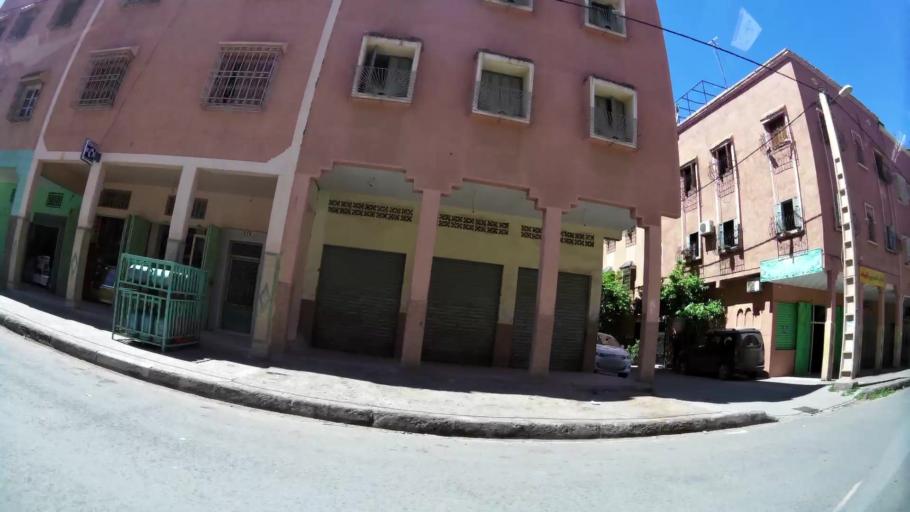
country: MA
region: Marrakech-Tensift-Al Haouz
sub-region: Marrakech
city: Marrakesh
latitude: 31.6359
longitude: -8.0657
